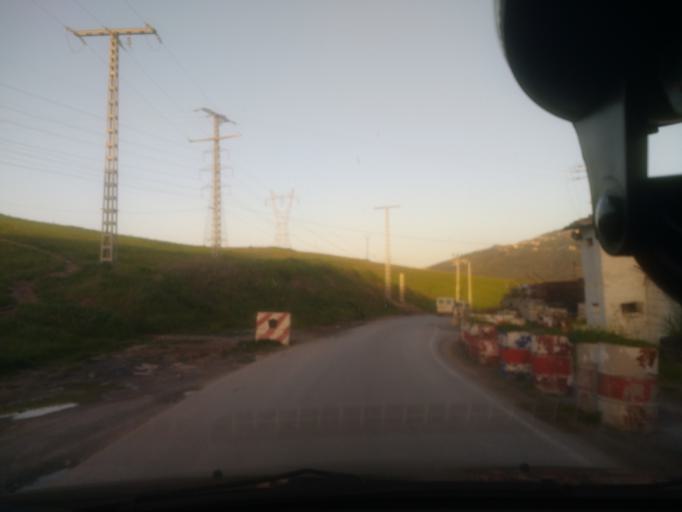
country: DZ
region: Boumerdes
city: Makouda
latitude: 36.7603
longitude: 4.0551
